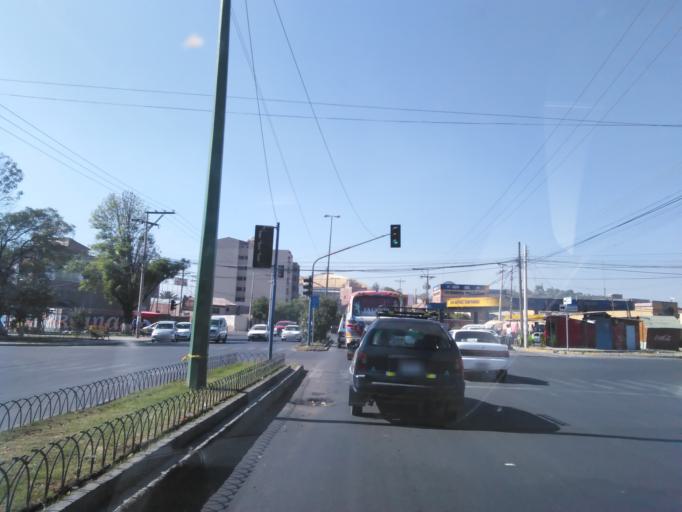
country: BO
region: Cochabamba
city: Cochabamba
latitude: -17.3989
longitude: -66.1646
